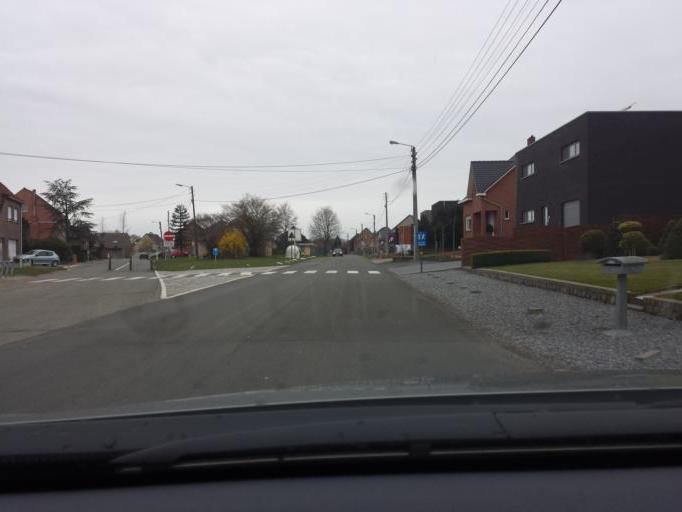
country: BE
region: Flanders
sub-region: Provincie Limburg
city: Tessenderlo
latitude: 51.0496
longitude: 5.1471
